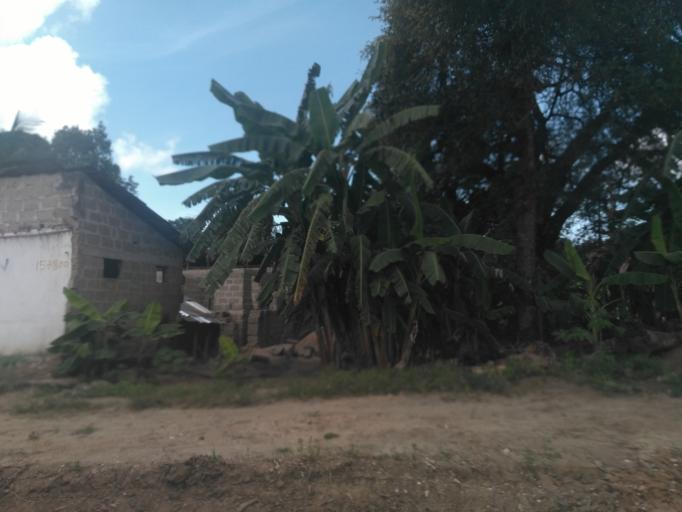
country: TZ
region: Zanzibar North
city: Gamba
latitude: -5.9752
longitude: 39.2976
